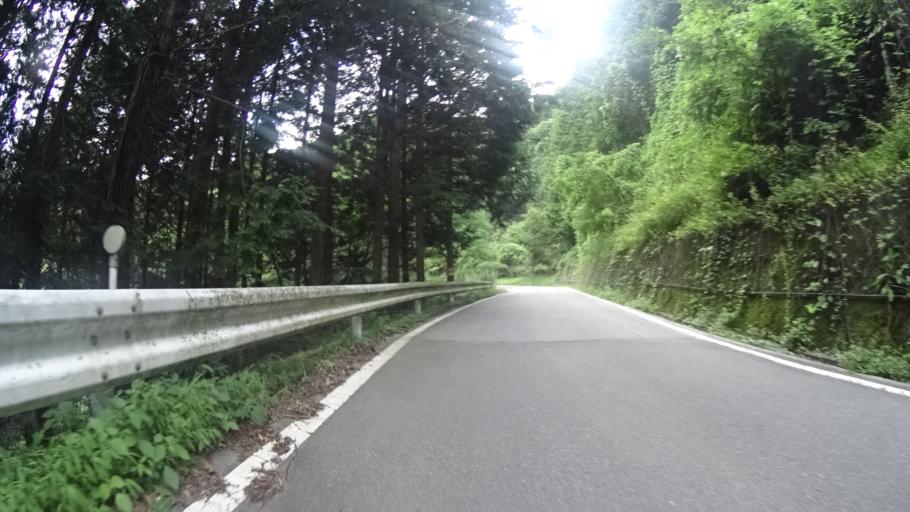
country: JP
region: Yamanashi
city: Enzan
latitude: 35.7887
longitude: 138.6900
